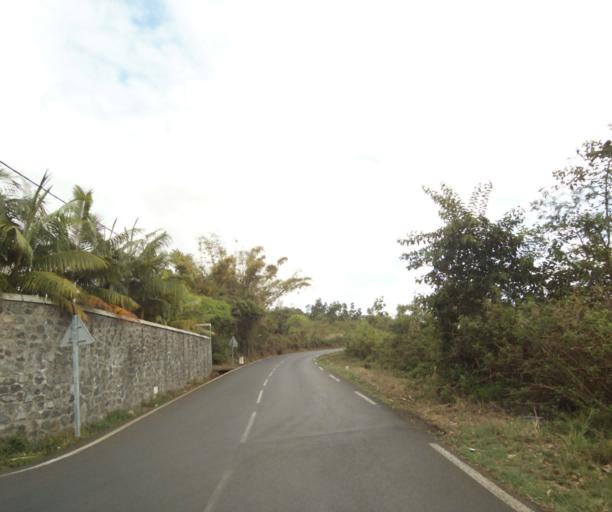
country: RE
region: Reunion
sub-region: Reunion
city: Trois-Bassins
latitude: -21.0566
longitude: 55.2828
